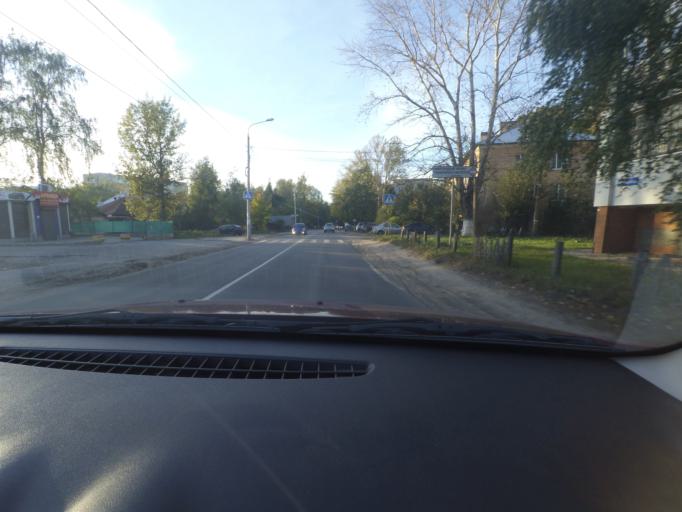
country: RU
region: Nizjnij Novgorod
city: Nizhniy Novgorod
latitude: 56.2617
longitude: 44.0021
